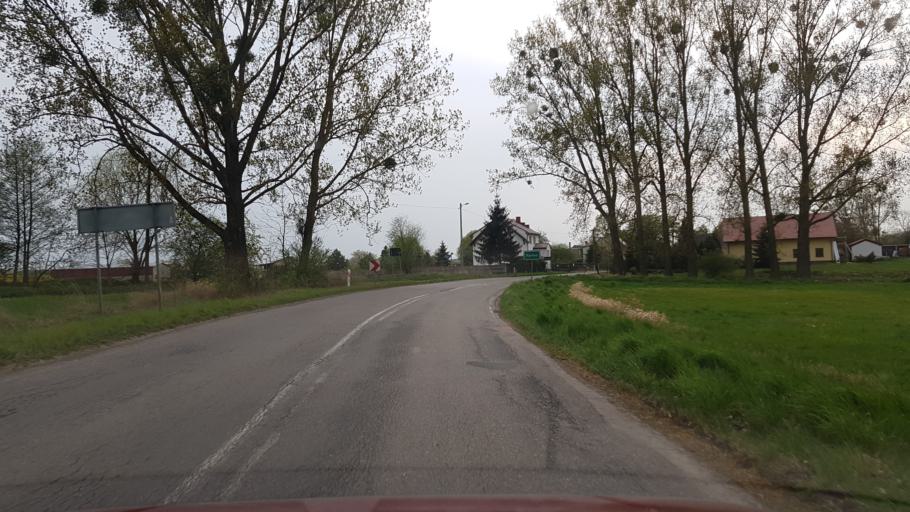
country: PL
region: West Pomeranian Voivodeship
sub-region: Powiat pyrzycki
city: Bielice
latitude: 53.2723
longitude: 14.6922
